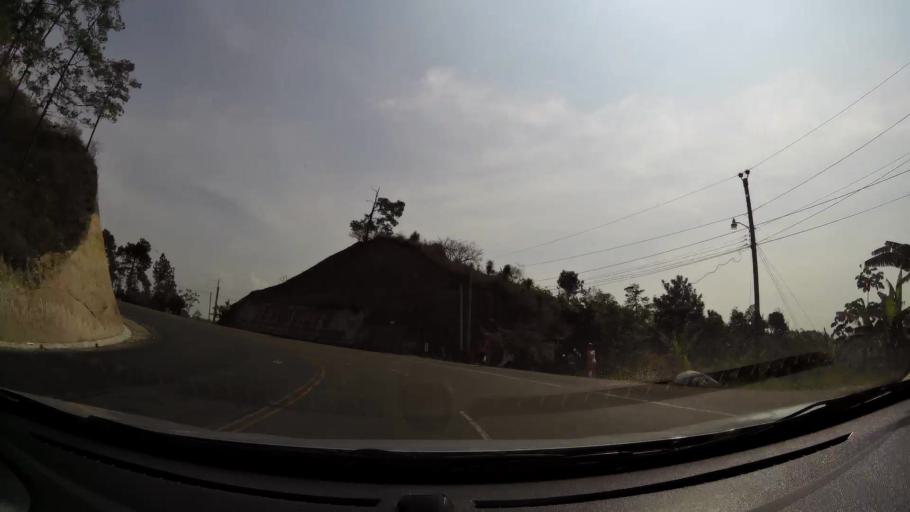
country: HN
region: Comayagua
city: Potrerillos
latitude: 14.5537
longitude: -87.8206
